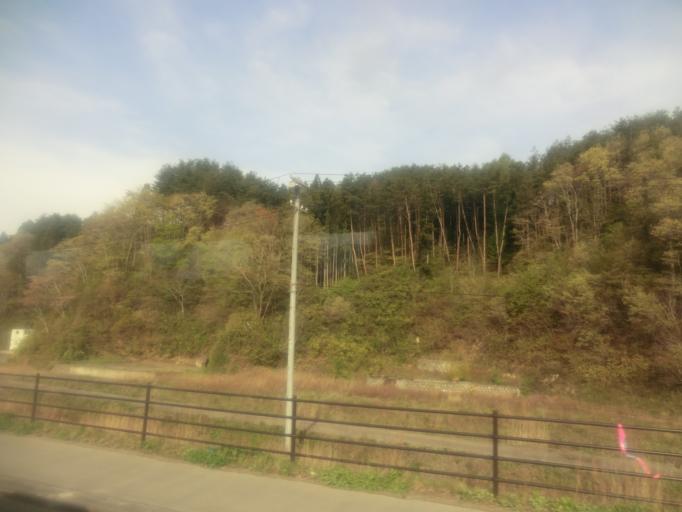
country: JP
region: Iwate
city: Miyako
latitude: 39.5877
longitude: 141.9459
